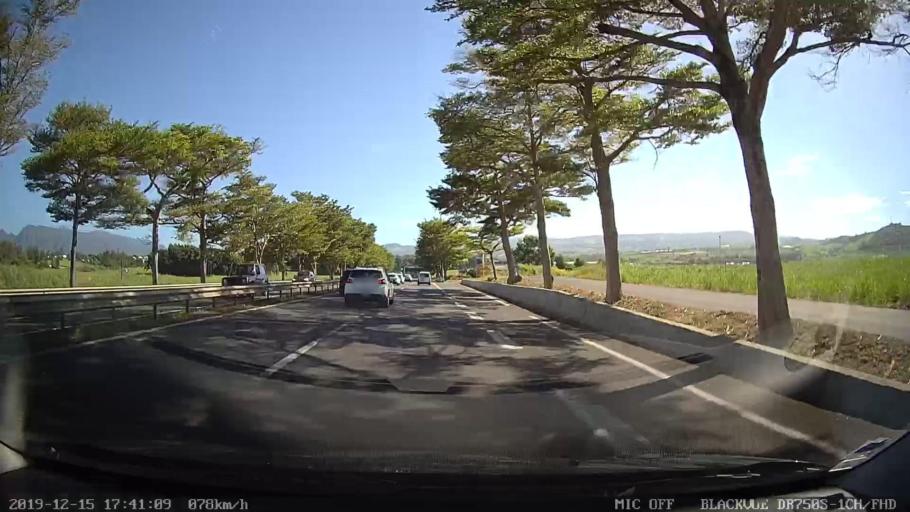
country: RE
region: Reunion
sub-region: Reunion
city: Saint-Pierre
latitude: -21.3129
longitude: 55.4950
